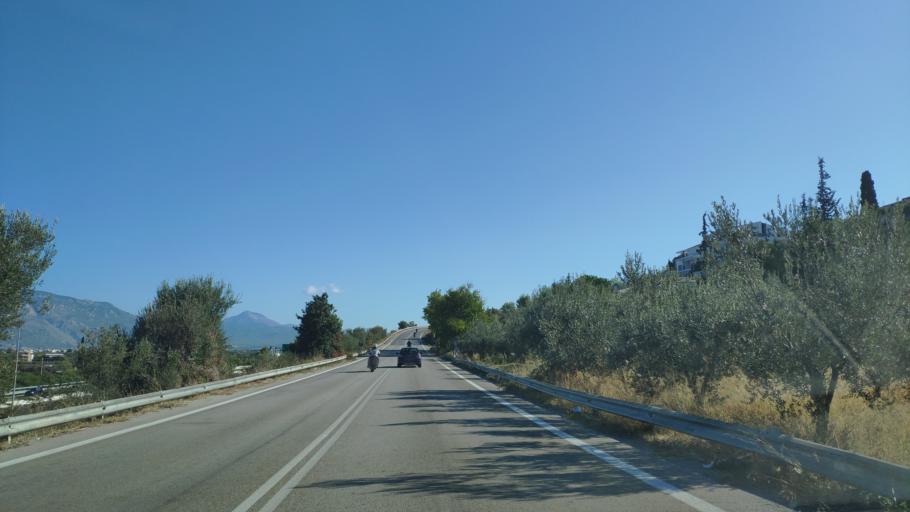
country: GR
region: Peloponnese
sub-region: Nomos Korinthias
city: Arkhaia Korinthos
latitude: 37.9149
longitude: 22.8899
